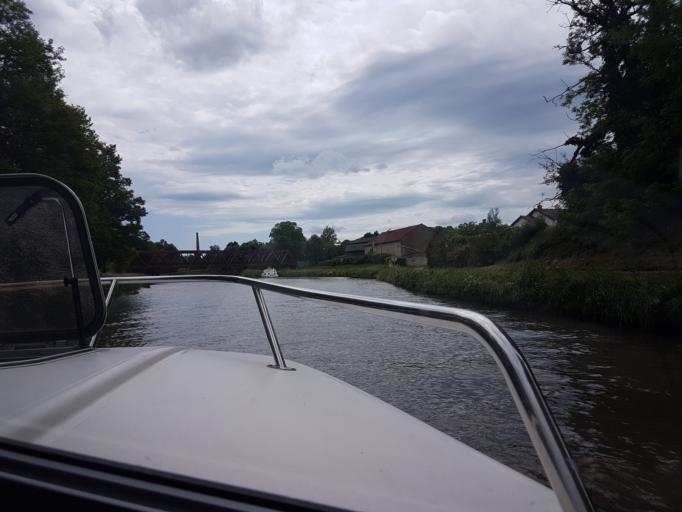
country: FR
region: Bourgogne
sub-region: Departement de la Nievre
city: Clamecy
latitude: 47.4795
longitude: 3.5242
